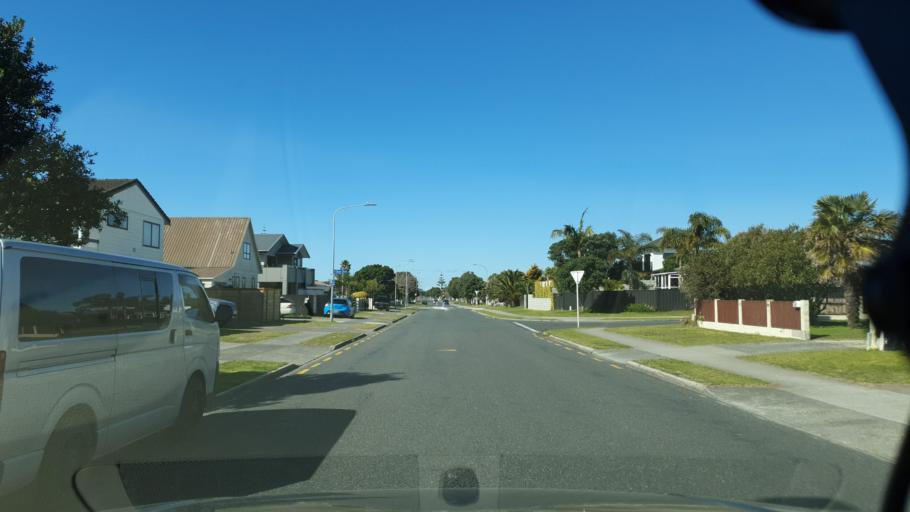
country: NZ
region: Bay of Plenty
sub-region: Tauranga City
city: Tauranga
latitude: -37.7019
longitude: 176.2935
